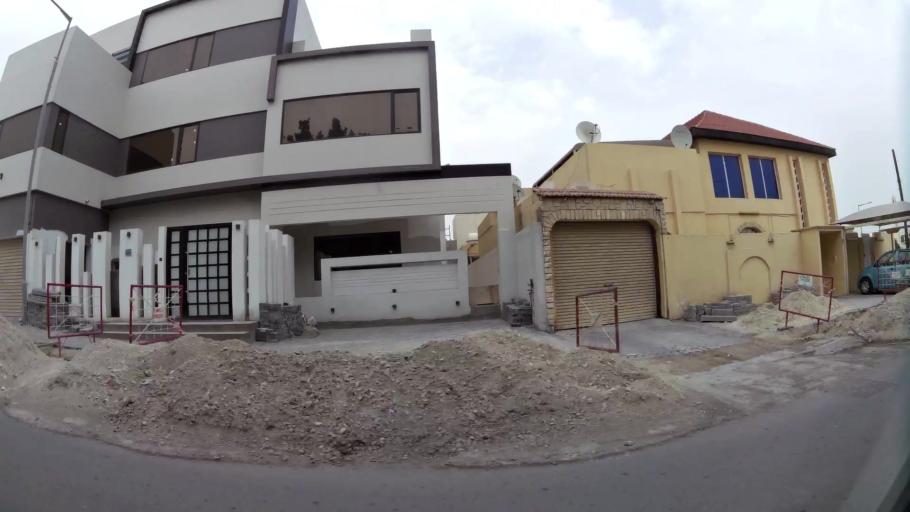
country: BH
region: Northern
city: Ar Rifa'
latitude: 26.1295
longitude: 50.5812
